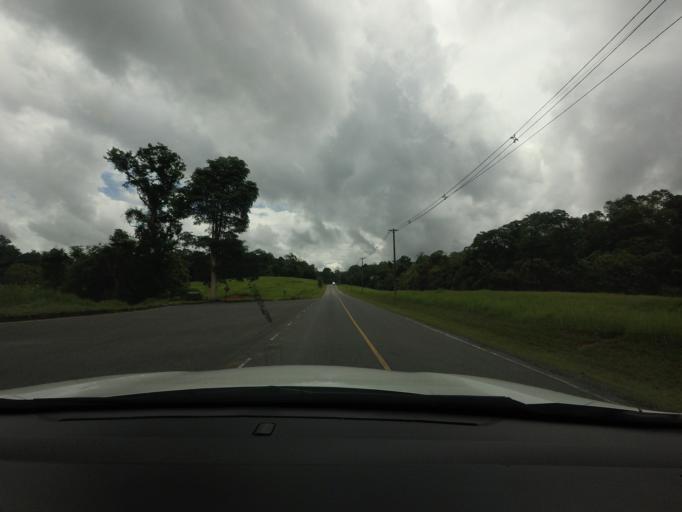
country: TH
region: Nakhon Ratchasima
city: Pak Chong
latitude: 14.4521
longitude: 101.3685
